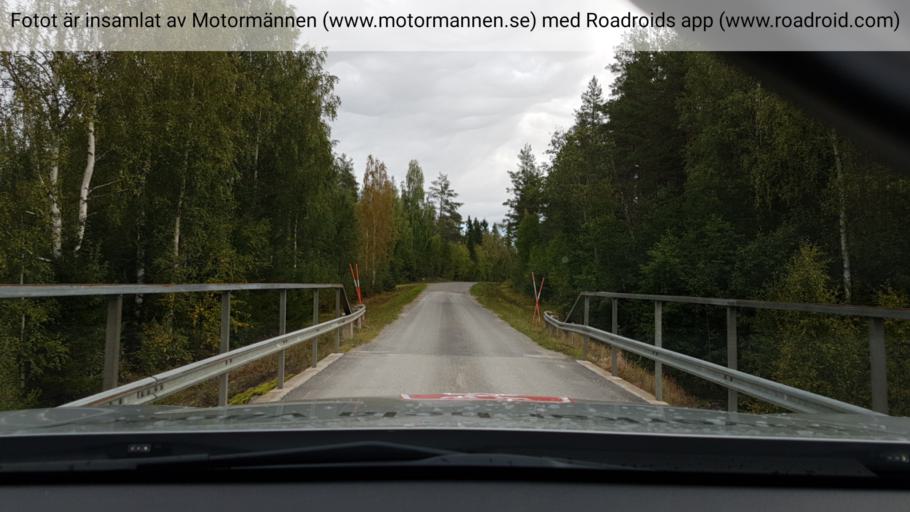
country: SE
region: Vaesterbotten
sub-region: Skelleftea Kommun
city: Byske
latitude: 65.1060
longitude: 21.1782
